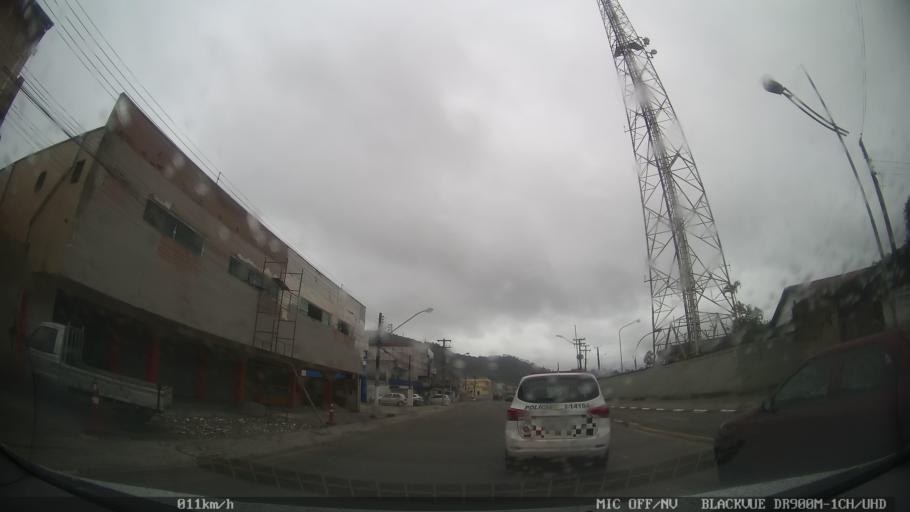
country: BR
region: Sao Paulo
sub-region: Juquia
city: Juquia
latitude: -24.3198
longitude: -47.6361
